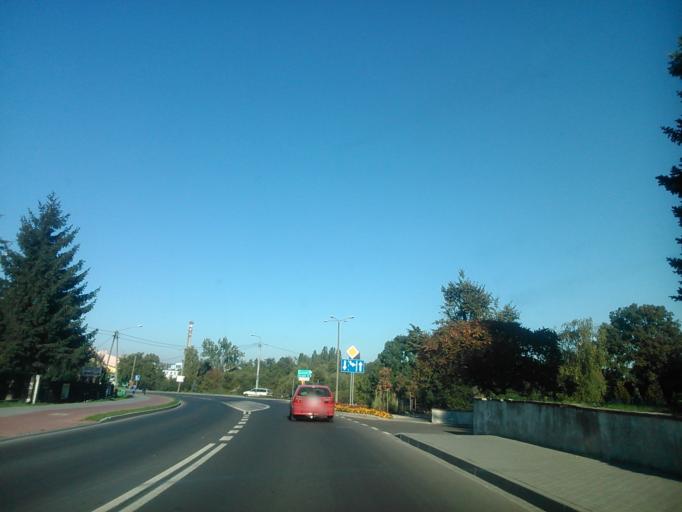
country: PL
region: Kujawsko-Pomorskie
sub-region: Powiat wabrzeski
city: Wabrzezno
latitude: 53.2779
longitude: 18.9641
